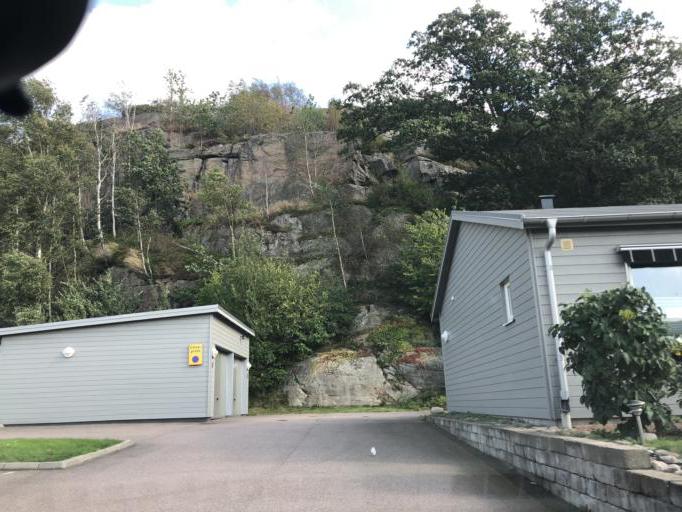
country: SE
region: Vaestra Goetaland
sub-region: Goteborg
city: Goeteborg
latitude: 57.7364
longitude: 11.9622
